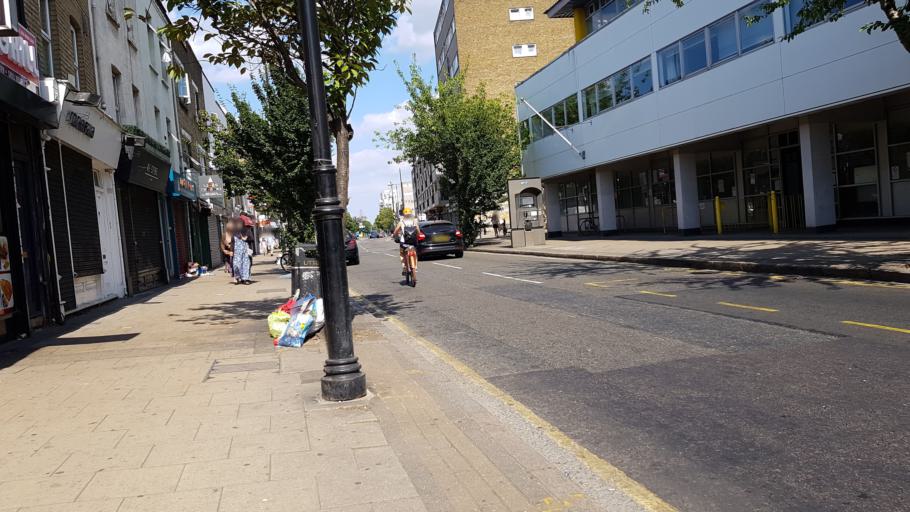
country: GB
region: England
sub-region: Greater London
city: Bethnal Green
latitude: 51.5283
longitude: -0.0503
